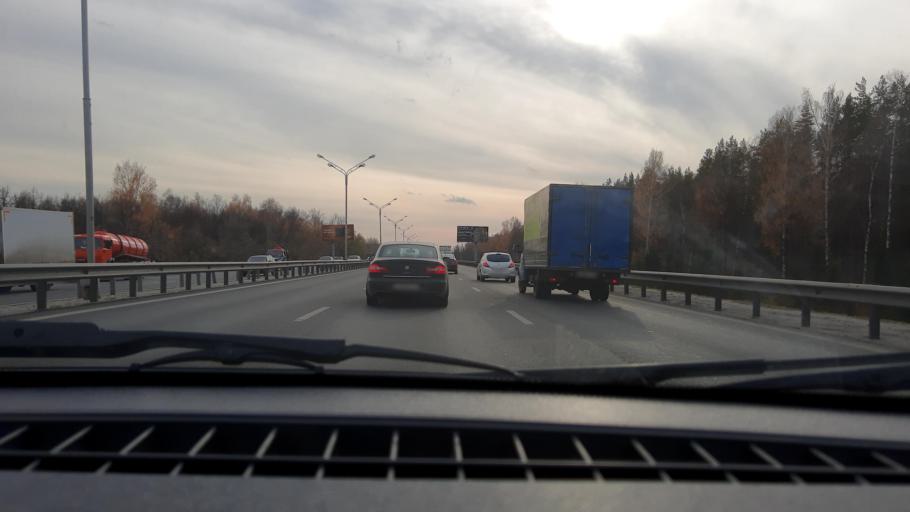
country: RU
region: Bashkortostan
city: Ufa
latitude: 54.6911
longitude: 55.9403
